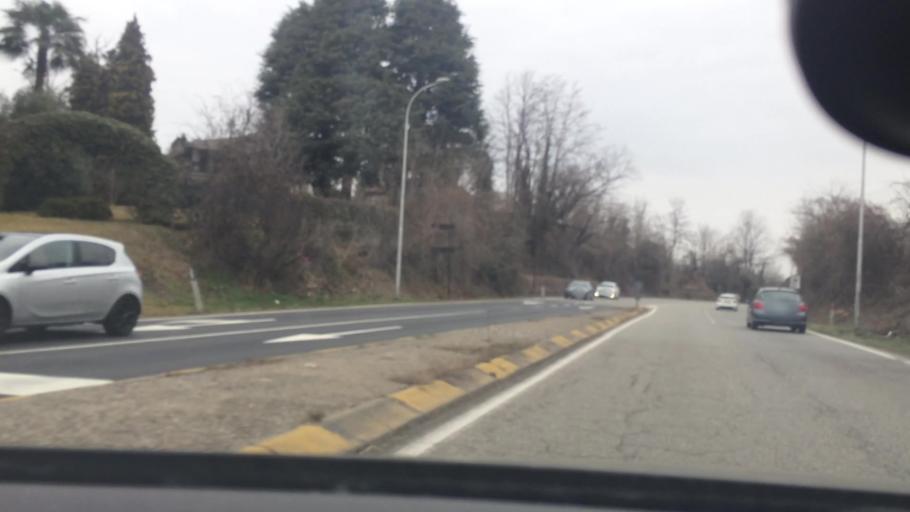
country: IT
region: Lombardy
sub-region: Provincia di Como
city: Inverigo
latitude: 45.7408
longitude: 9.2152
